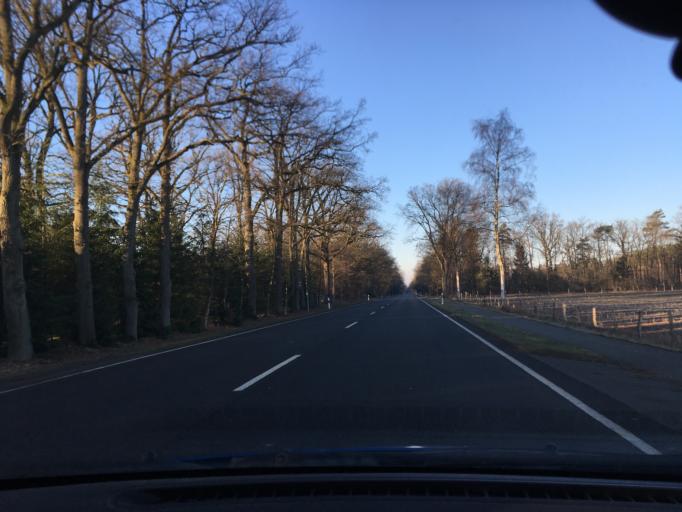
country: DE
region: Lower Saxony
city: Handeloh
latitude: 53.1918
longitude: 9.8314
